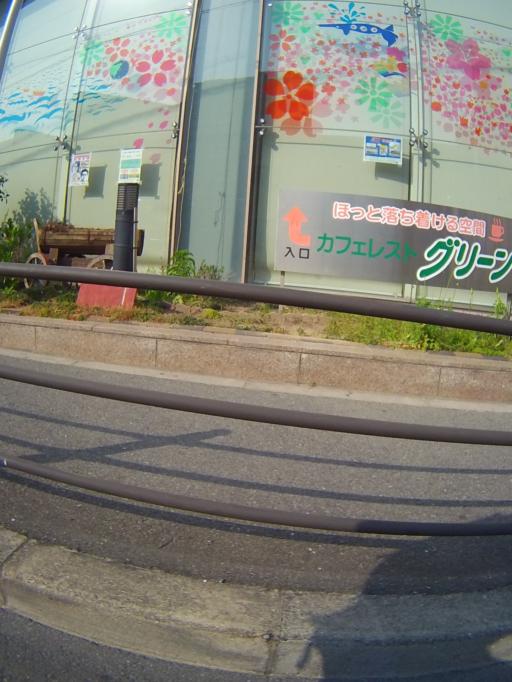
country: JP
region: Osaka
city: Osaka-shi
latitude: 34.6836
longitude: 135.4644
